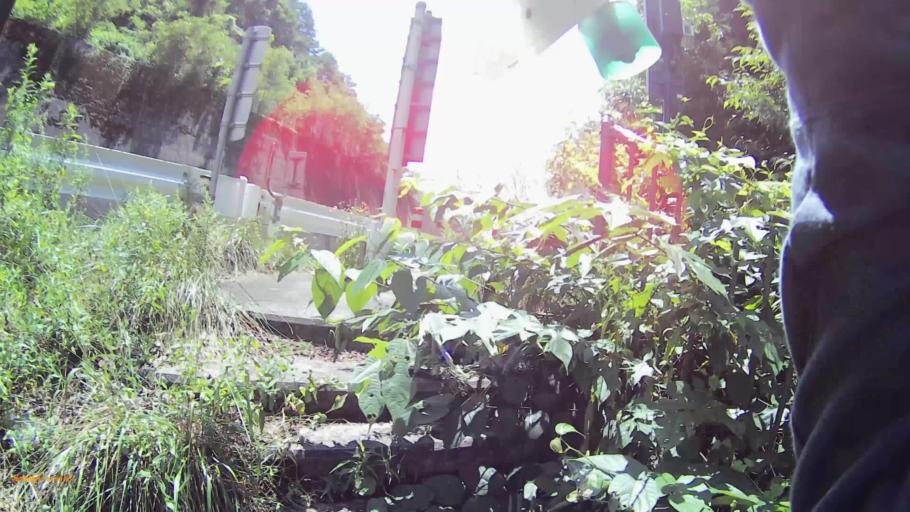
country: JP
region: Nagano
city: Ina
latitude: 35.8310
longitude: 137.6821
